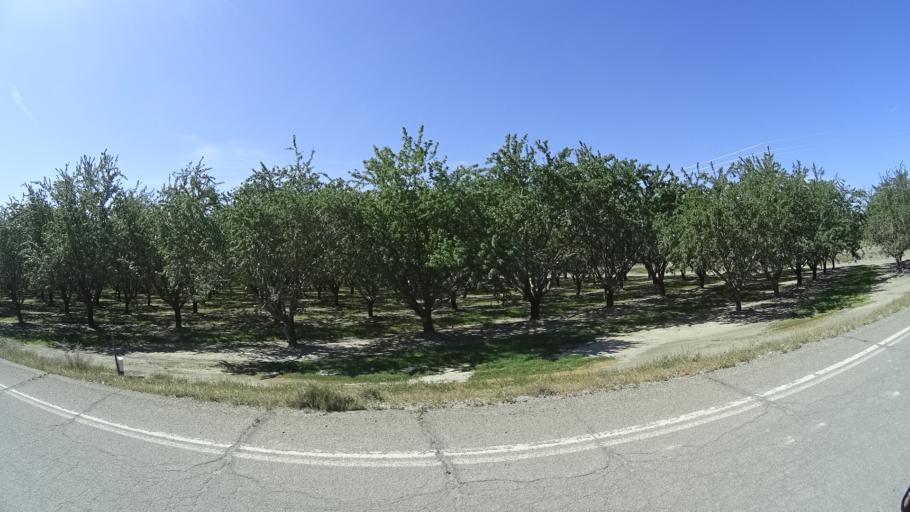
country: US
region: California
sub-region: Glenn County
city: Hamilton City
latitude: 39.7422
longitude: -122.1035
